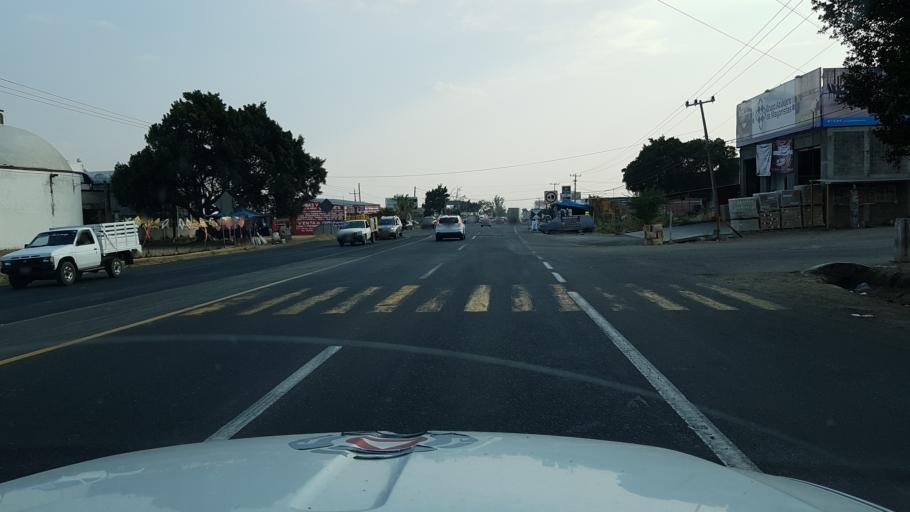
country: MX
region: Morelos
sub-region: Atlatlahucan
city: Colonia San Francisco
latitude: 18.8927
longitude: -98.9119
